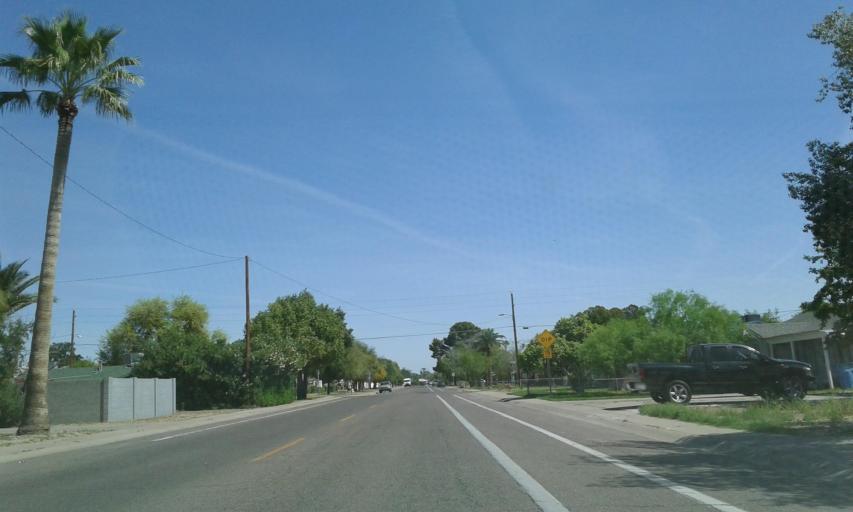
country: US
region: Arizona
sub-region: Maricopa County
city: Phoenix
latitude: 33.5023
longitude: -112.0968
